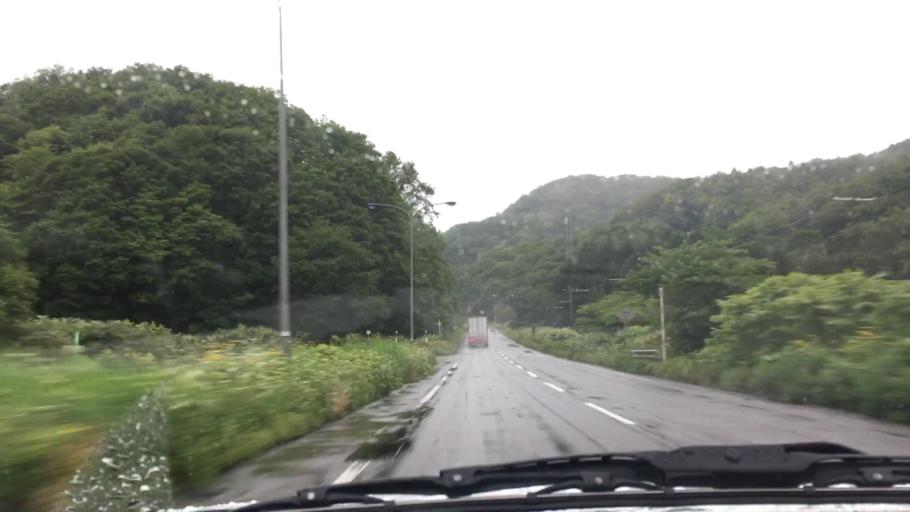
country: JP
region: Hokkaido
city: Niseko Town
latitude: 42.6014
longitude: 140.6214
